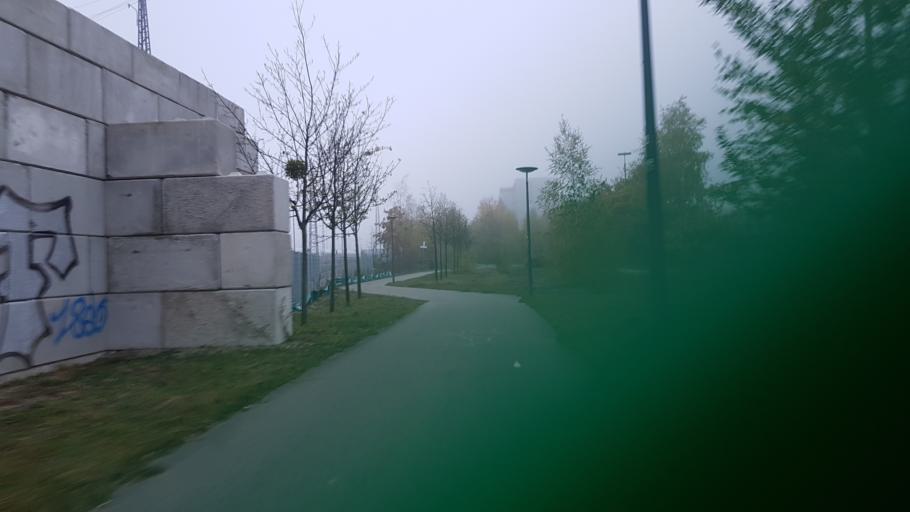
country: DE
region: Bavaria
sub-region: Upper Bavaria
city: Pasing
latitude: 48.1452
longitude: 11.5106
